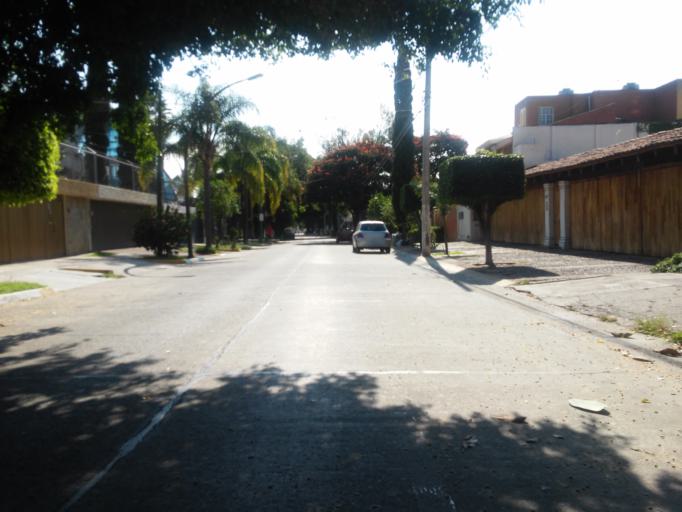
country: MX
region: Jalisco
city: Guadalajara
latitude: 20.6597
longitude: -103.4002
